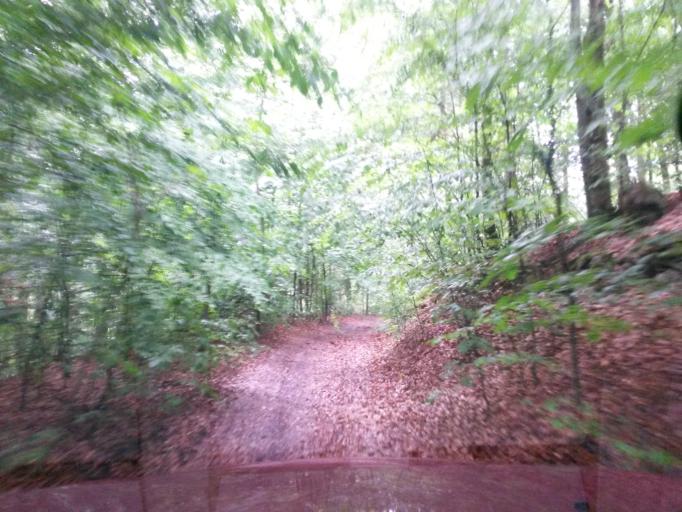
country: SK
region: Kosicky
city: Kosice
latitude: 48.7223
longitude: 21.1549
